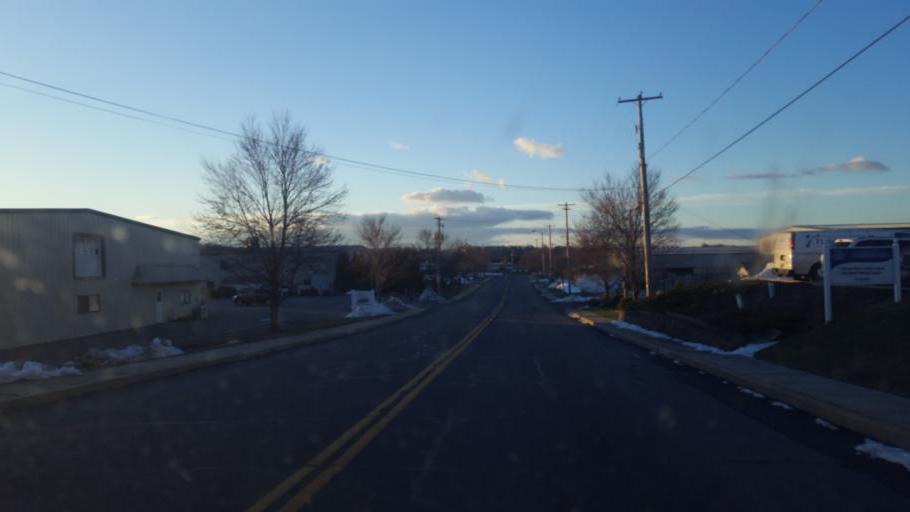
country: US
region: Pennsylvania
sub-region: Lancaster County
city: New Holland
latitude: 40.0919
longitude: -76.0893
